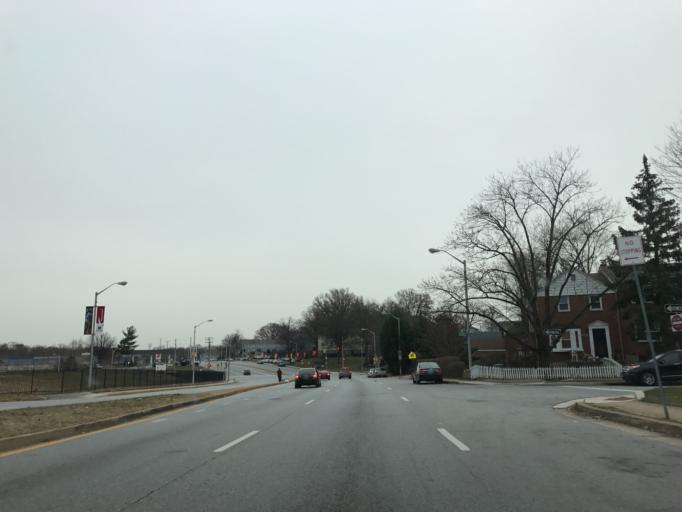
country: US
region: Maryland
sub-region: Baltimore County
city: Towson
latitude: 39.3660
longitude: -76.5875
